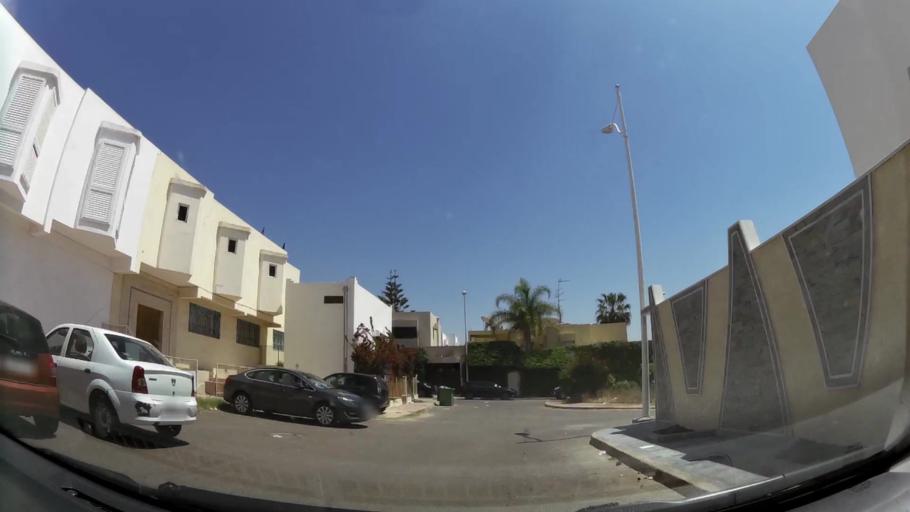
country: MA
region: Souss-Massa-Draa
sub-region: Agadir-Ida-ou-Tnan
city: Agadir
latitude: 30.4354
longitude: -9.5838
